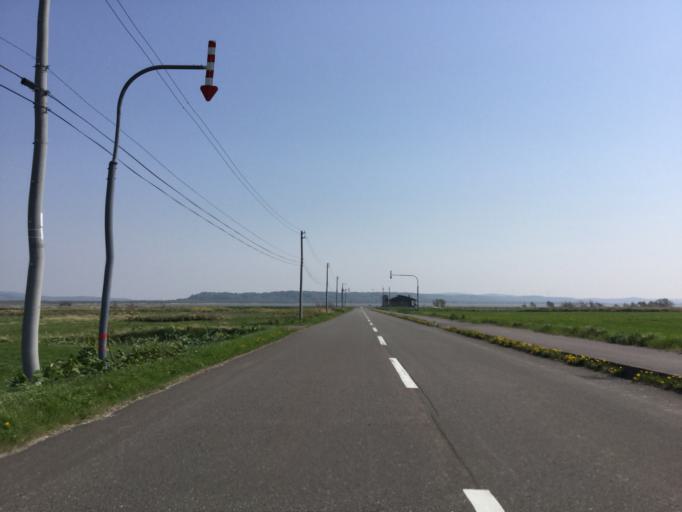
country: JP
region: Hokkaido
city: Makubetsu
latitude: 45.3937
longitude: 141.7673
